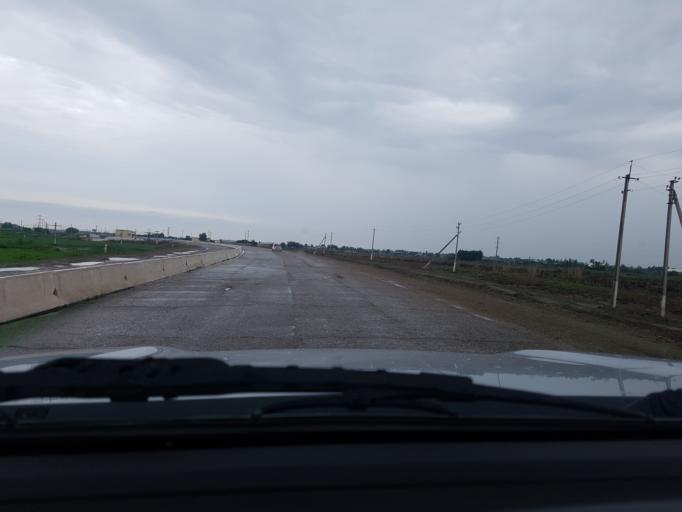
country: UZ
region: Bukhara
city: Olot
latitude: 39.3680
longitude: 63.7977
